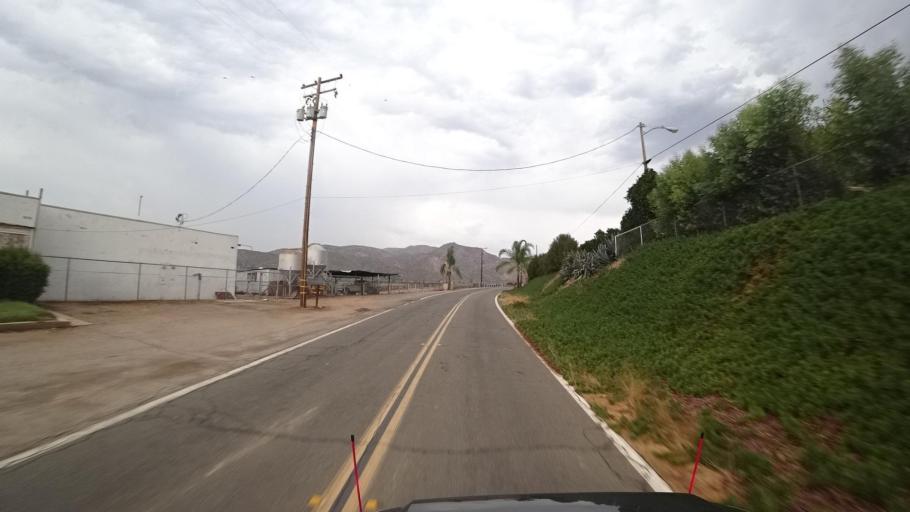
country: US
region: California
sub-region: San Diego County
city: San Pasqual
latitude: 33.0774
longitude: -116.9740
